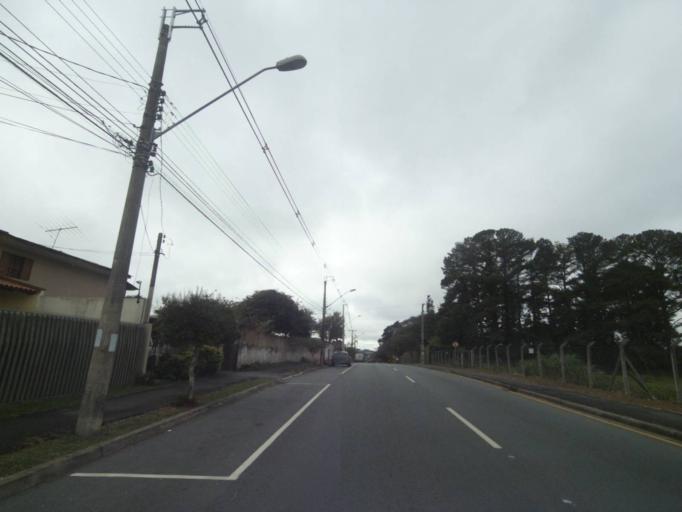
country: BR
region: Parana
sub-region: Curitiba
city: Curitiba
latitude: -25.5047
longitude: -49.2932
